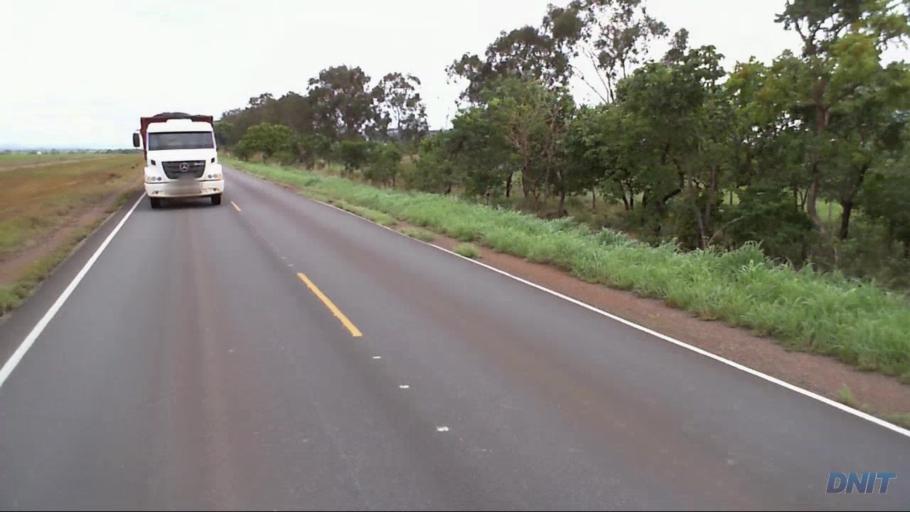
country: BR
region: Goias
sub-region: Padre Bernardo
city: Padre Bernardo
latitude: -15.3270
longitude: -48.2313
